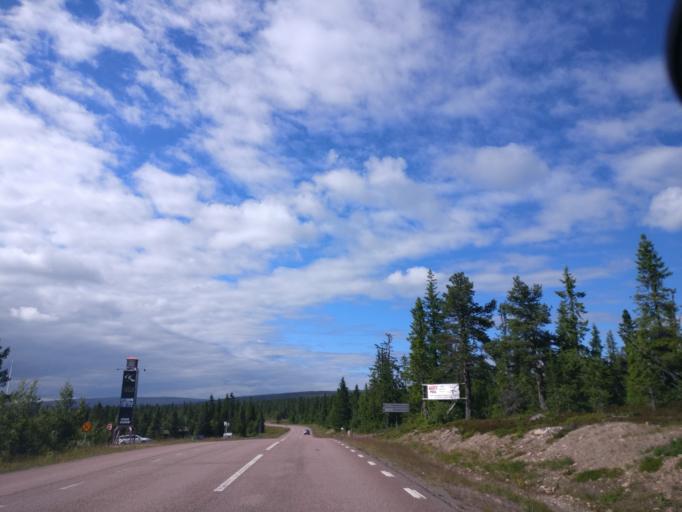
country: SE
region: Dalarna
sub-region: Malung-Saelens kommun
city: Malung
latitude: 61.1599
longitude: 13.1117
